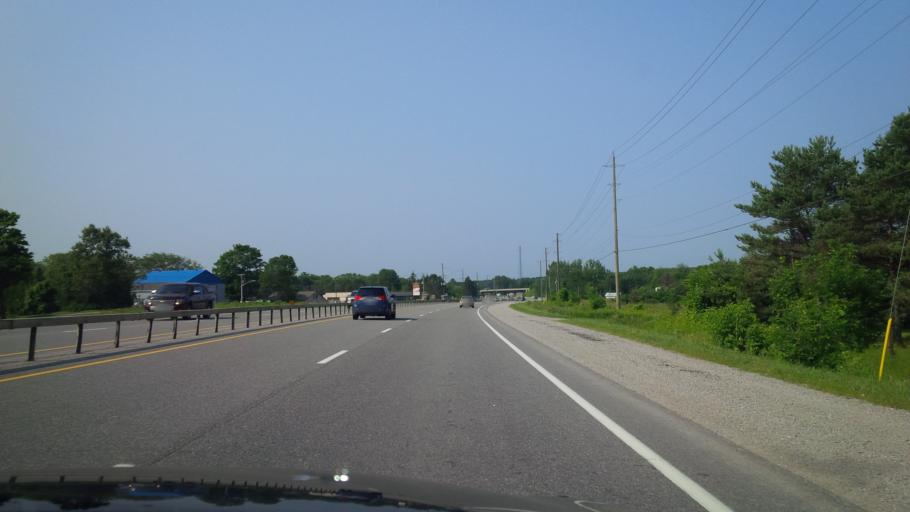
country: CA
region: Ontario
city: Orillia
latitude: 44.7063
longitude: -79.3884
